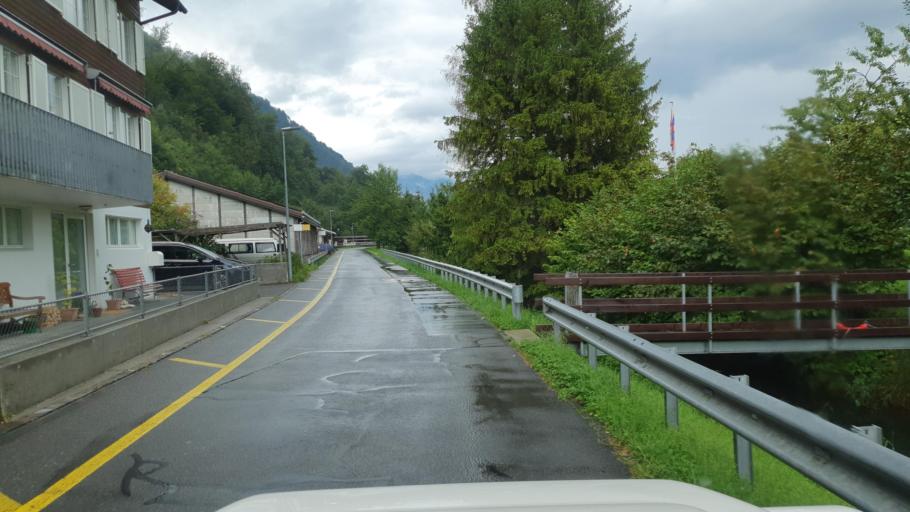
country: CH
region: Nidwalden
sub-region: Nidwalden
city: Stans
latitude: 46.9684
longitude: 8.3615
